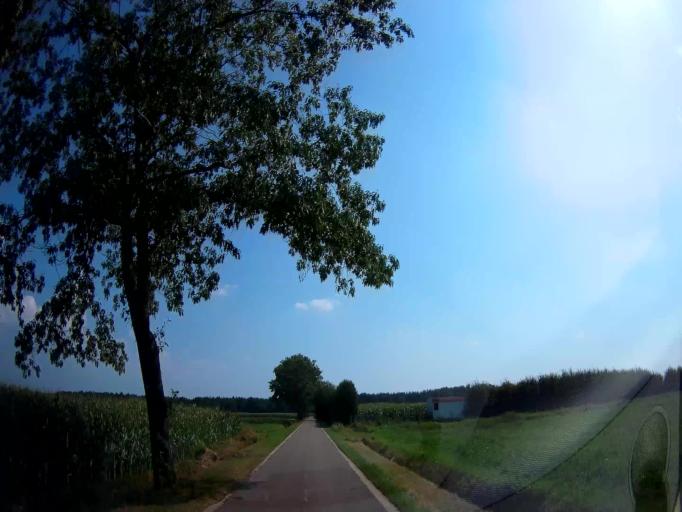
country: BE
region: Flanders
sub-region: Provincie Antwerpen
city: Retie
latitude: 51.2704
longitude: 5.0408
